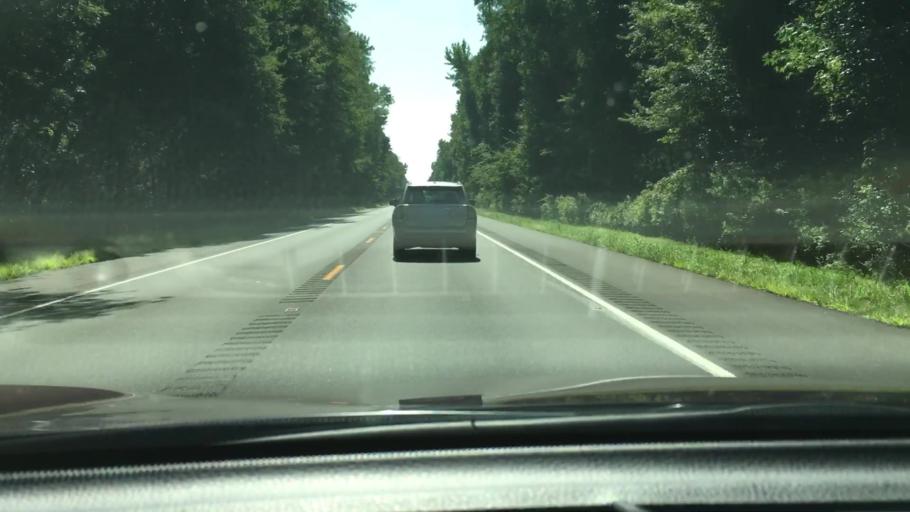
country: US
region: New Jersey
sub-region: Cape May County
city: Woodbine
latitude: 39.3331
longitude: -74.8800
